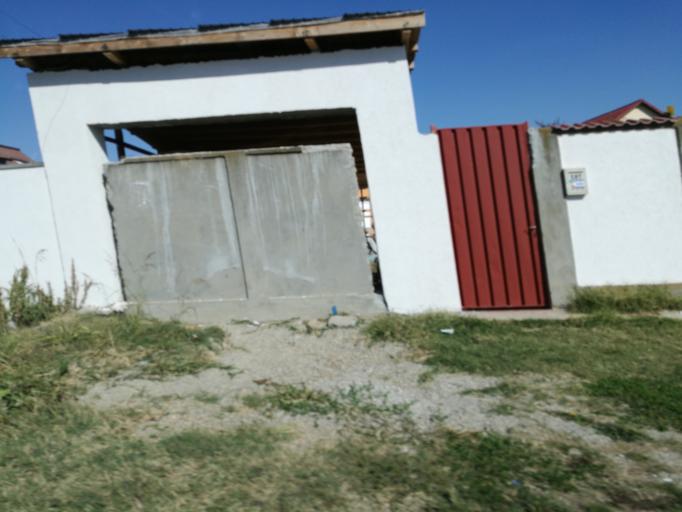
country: RO
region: Ilfov
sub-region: Comuna Dragomiresti-Vale
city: Dragomiresti-Vale
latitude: 44.4682
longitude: 25.9225
